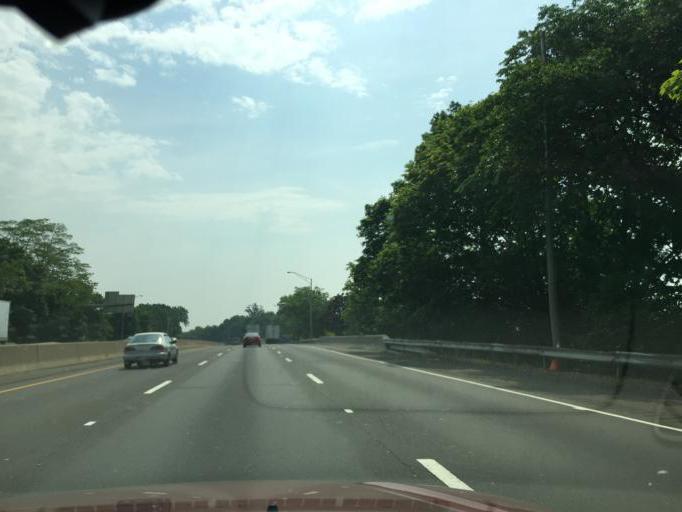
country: US
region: Connecticut
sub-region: Fairfield County
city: Riverside
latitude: 41.0445
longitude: -73.5592
